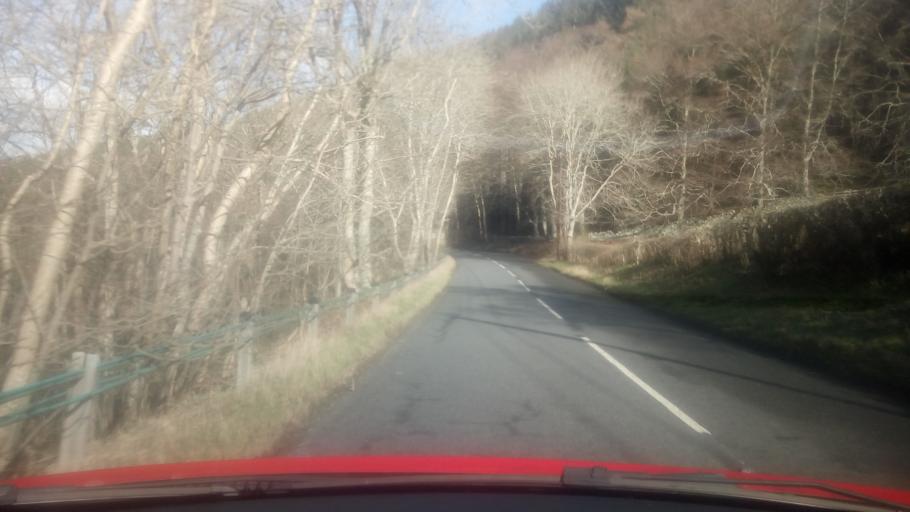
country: GB
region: Scotland
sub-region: The Scottish Borders
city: Selkirk
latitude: 55.5969
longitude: -2.8657
